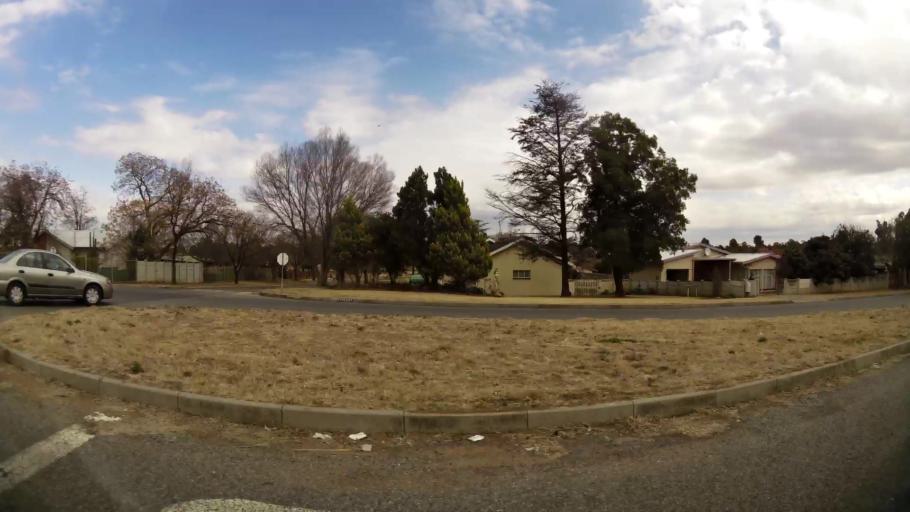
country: ZA
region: Orange Free State
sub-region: Fezile Dabi District Municipality
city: Kroonstad
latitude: -27.6433
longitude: 27.2275
